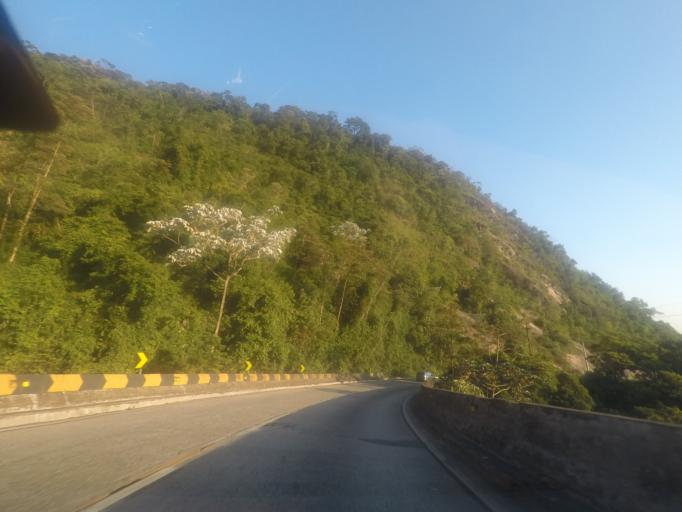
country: BR
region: Rio de Janeiro
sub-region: Petropolis
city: Petropolis
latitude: -22.5320
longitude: -43.2339
